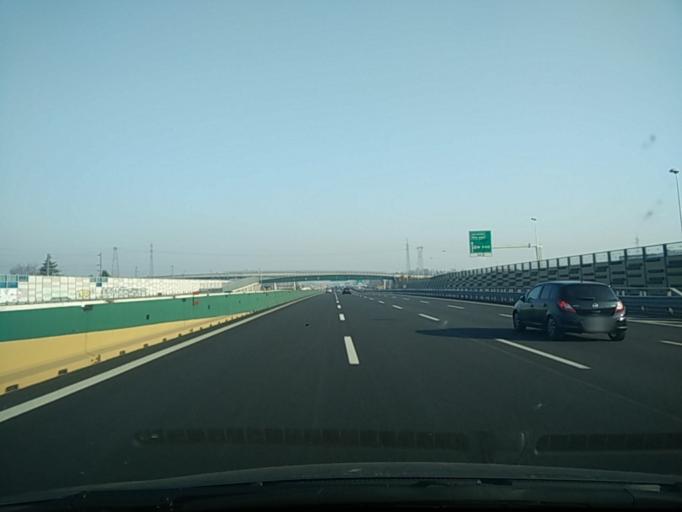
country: IT
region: Lombardy
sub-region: Citta metropolitana di Milano
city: Cornaredo
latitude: 45.5084
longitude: 9.0249
